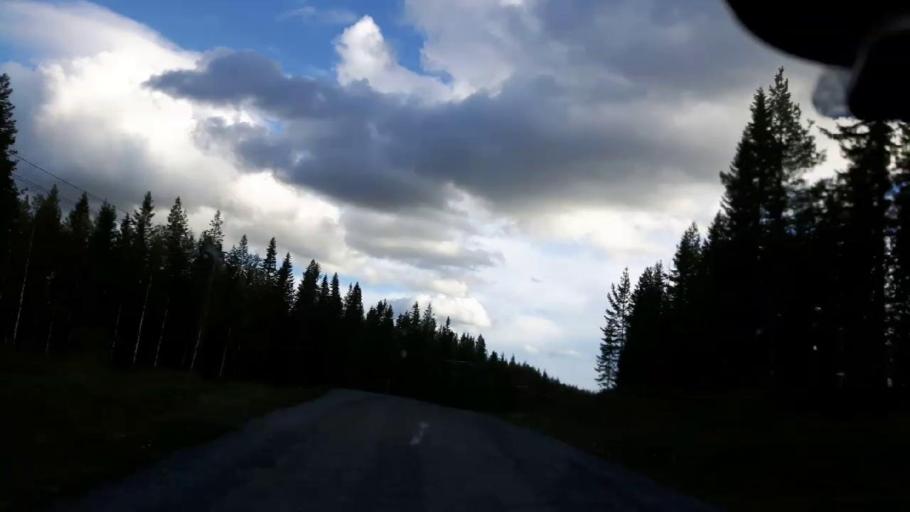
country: SE
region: Jaemtland
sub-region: Stroemsunds Kommun
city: Stroemsund
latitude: 63.3276
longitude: 15.5803
